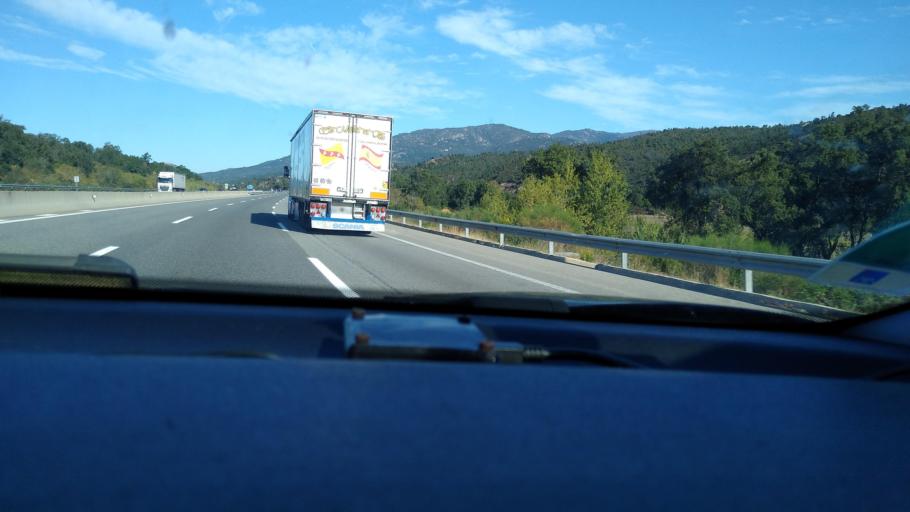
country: ES
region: Catalonia
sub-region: Provincia de Girona
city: Capmany
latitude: 42.3777
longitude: 2.8863
